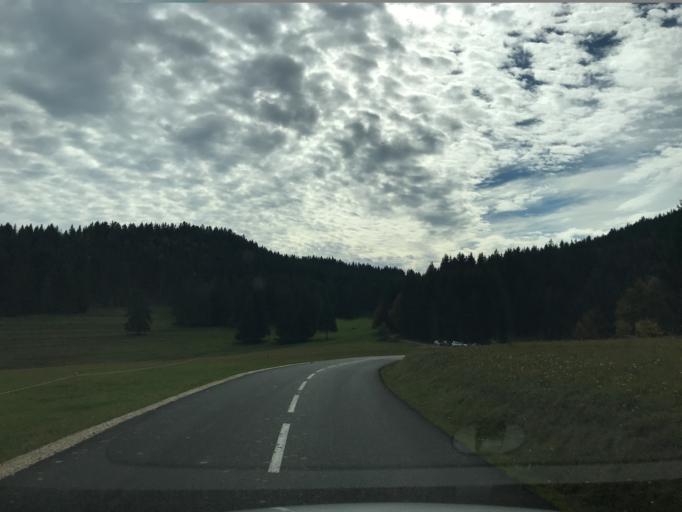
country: FR
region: Rhone-Alpes
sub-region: Departement de la Savoie
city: Vimines
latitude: 45.4558
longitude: 5.8587
